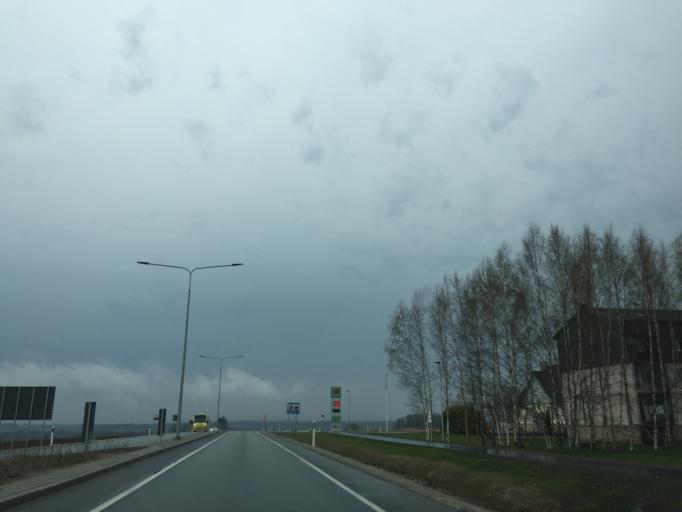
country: EE
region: Tartu
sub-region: UElenurme vald
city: Ulenurme
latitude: 58.2385
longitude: 26.6898
